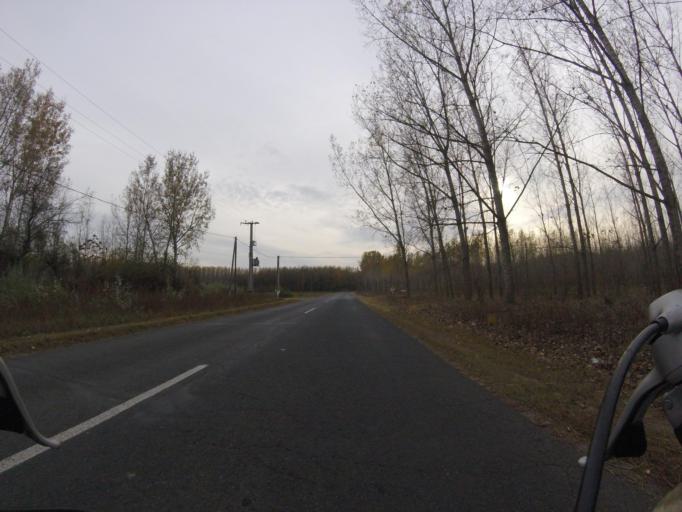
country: HU
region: Pest
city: Csemo
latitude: 47.1221
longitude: 19.6531
